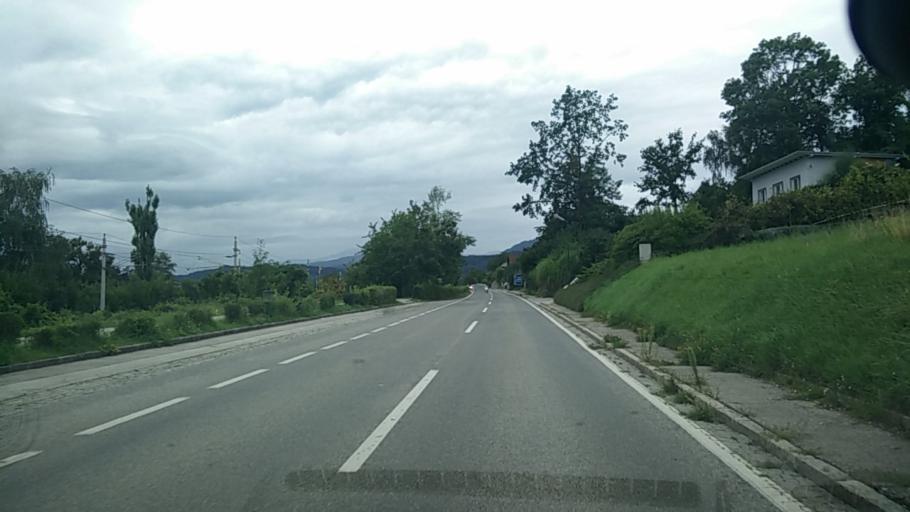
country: AT
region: Carinthia
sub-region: Politischer Bezirk Klagenfurt Land
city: Maria Worth
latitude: 46.6268
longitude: 14.1755
